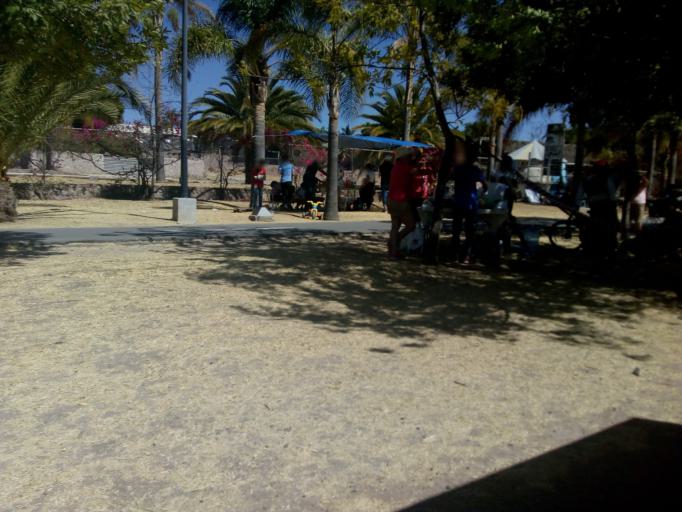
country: MX
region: Guanajuato
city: Leon
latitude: 21.1791
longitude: -101.6788
